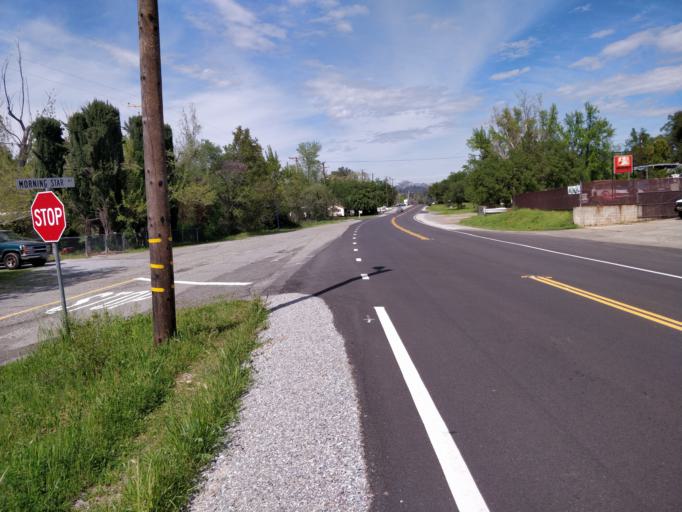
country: US
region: California
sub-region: Shasta County
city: Shasta Lake
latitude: 40.6763
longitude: -122.3535
